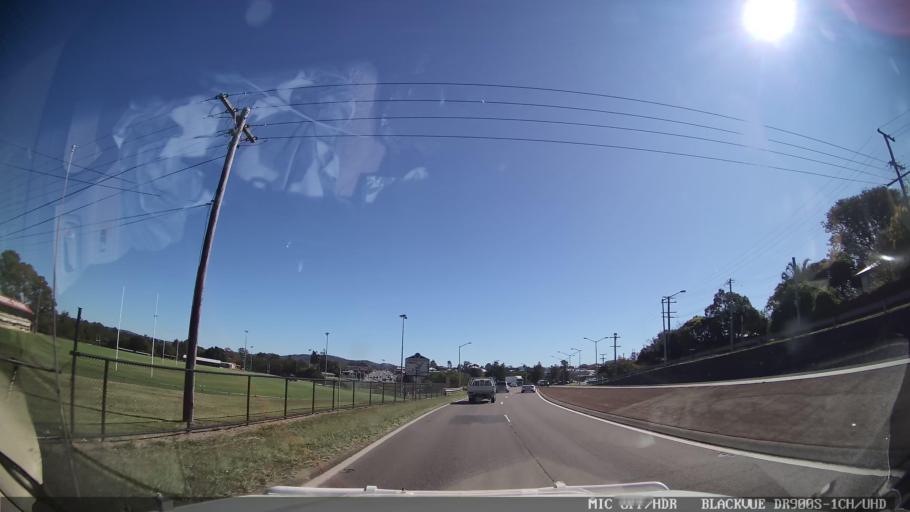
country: AU
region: Queensland
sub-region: Gympie Regional Council
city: Gympie
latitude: -26.1953
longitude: 152.6618
